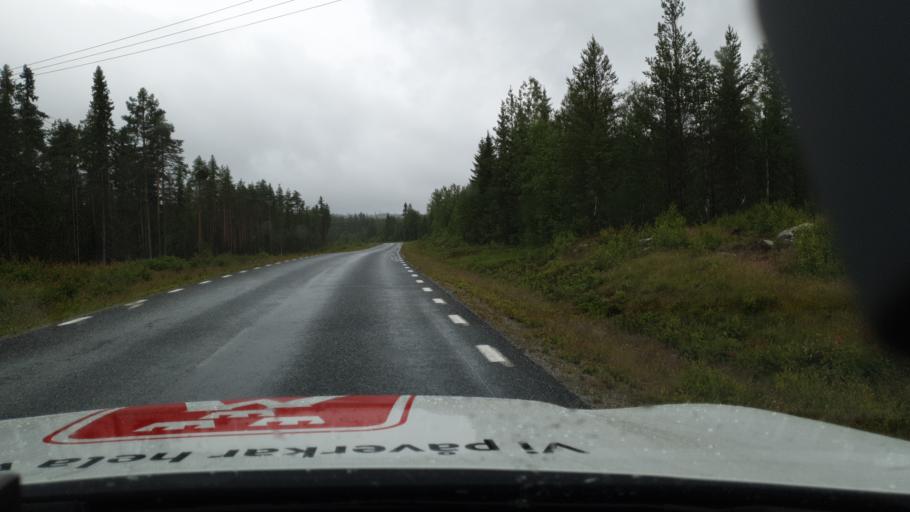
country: SE
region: Vaesterbotten
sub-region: Asele Kommun
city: Insjon
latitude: 64.3148
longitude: 17.6996
